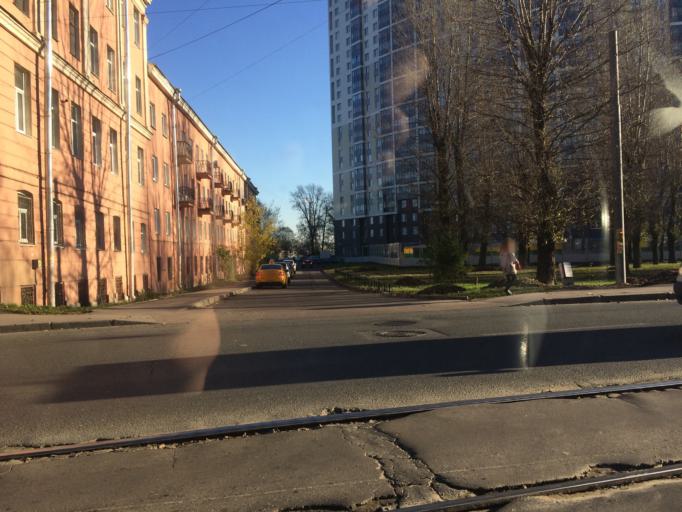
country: RU
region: St.-Petersburg
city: Obukhovo
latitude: 59.8674
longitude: 30.4658
